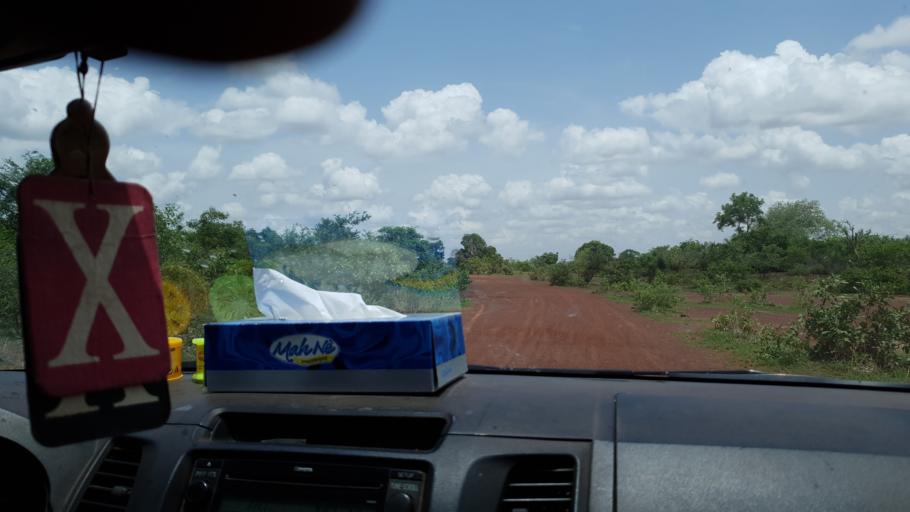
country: ML
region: Koulikoro
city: Banamba
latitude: 13.3782
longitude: -7.2148
